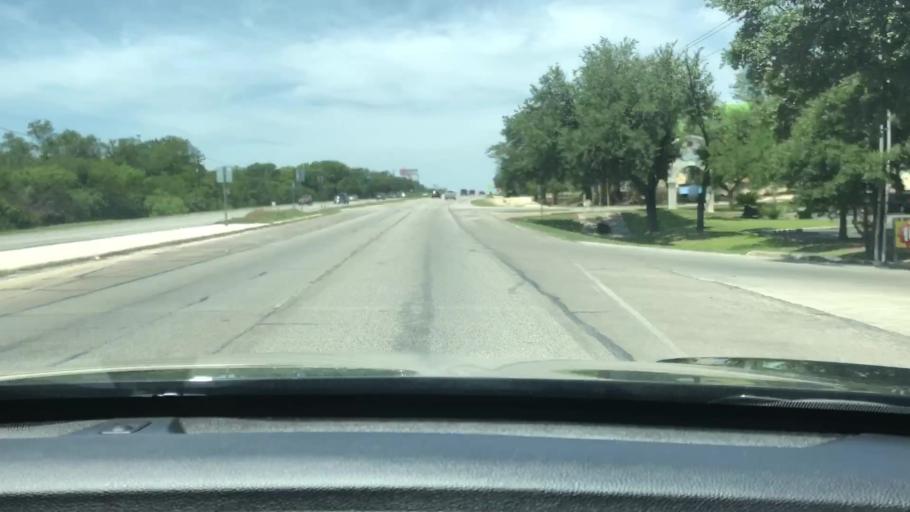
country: US
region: Texas
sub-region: Bexar County
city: Helotes
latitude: 29.5436
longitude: -98.6573
